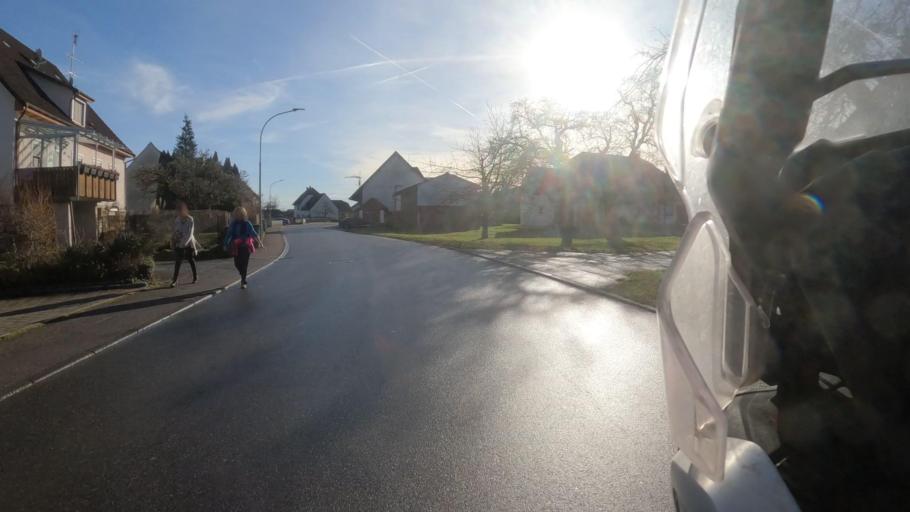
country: DE
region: Baden-Wuerttemberg
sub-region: Freiburg Region
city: Neuhausen
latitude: 47.8357
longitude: 8.7773
